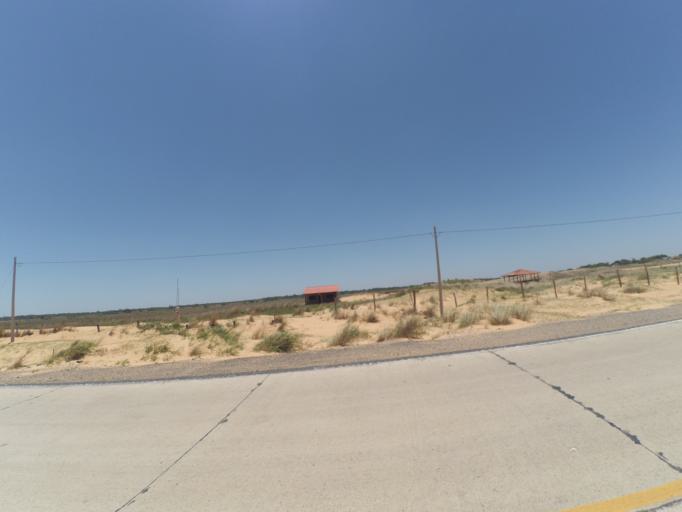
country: BO
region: Santa Cruz
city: Santa Cruz de la Sierra
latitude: -17.8010
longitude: -63.2756
